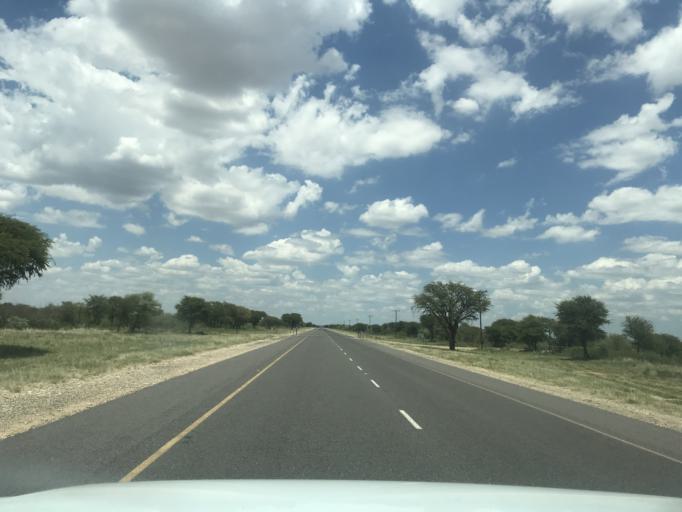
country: BW
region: South East
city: Janeng
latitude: -25.7026
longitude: 25.1240
